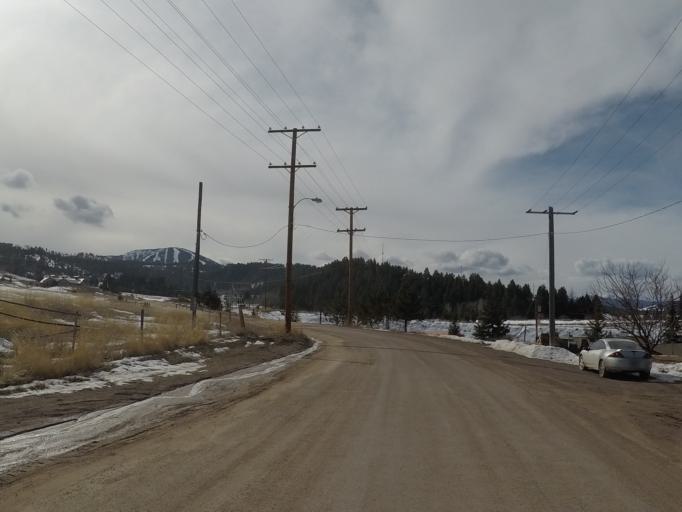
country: US
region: Montana
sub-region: Granite County
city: Philipsburg
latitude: 46.3286
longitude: -113.2935
